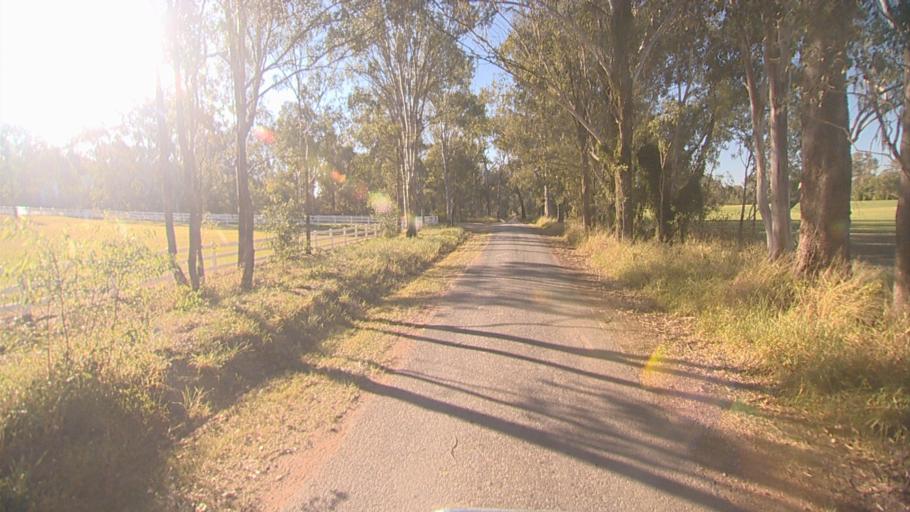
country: AU
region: Queensland
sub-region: Logan
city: North Maclean
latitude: -27.7758
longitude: 153.0379
